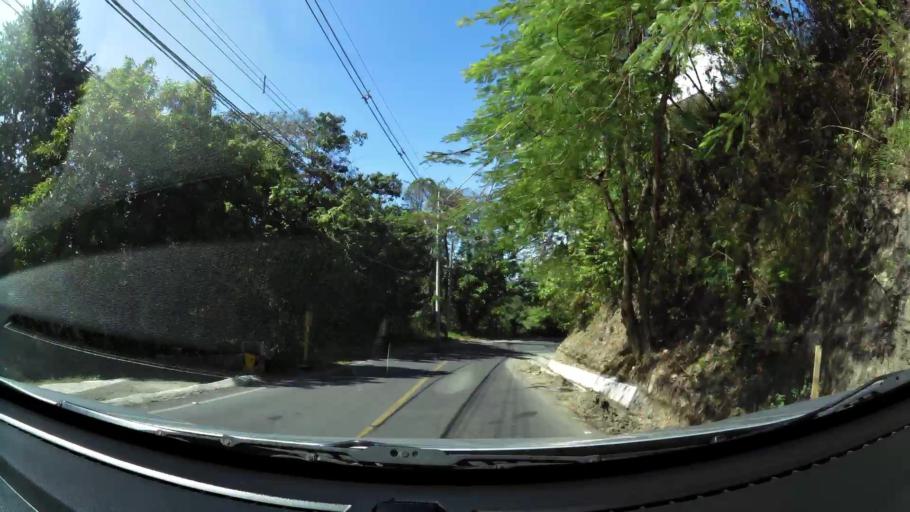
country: CR
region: Puntarenas
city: Quepos
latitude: 9.4251
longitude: -84.1600
